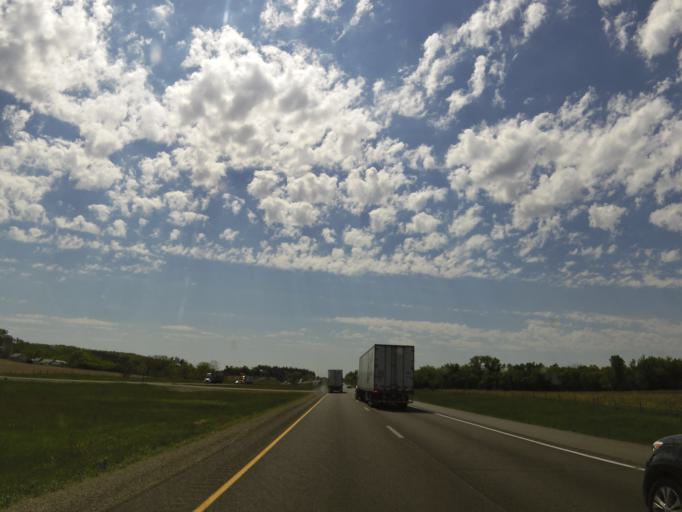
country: US
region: Wisconsin
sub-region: Eau Claire County
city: Altoona
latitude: 44.7406
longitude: -91.3764
